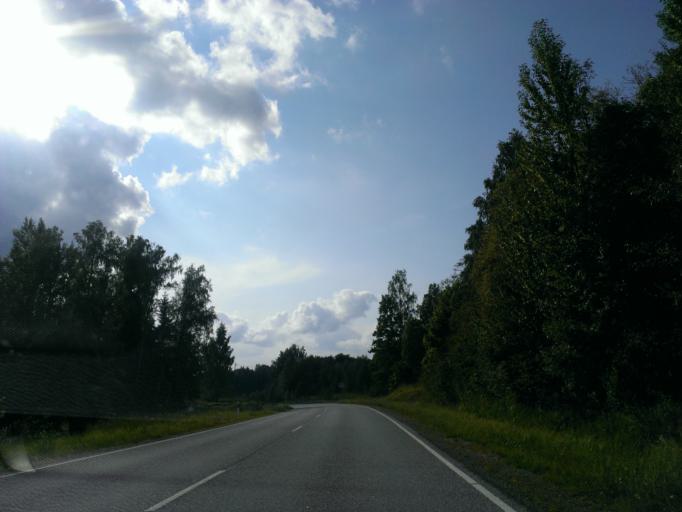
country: LV
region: Priekuli
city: Priekuli
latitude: 57.2937
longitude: 25.4653
